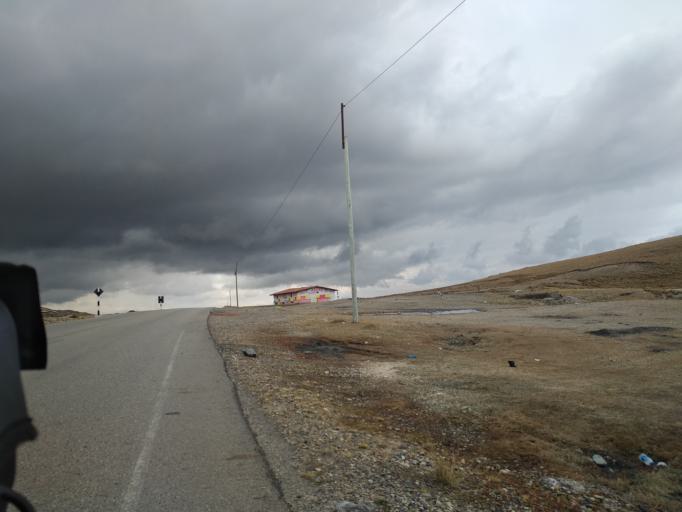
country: PE
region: La Libertad
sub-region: Provincia de Santiago de Chuco
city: Quiruvilca
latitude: -7.9905
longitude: -78.2870
